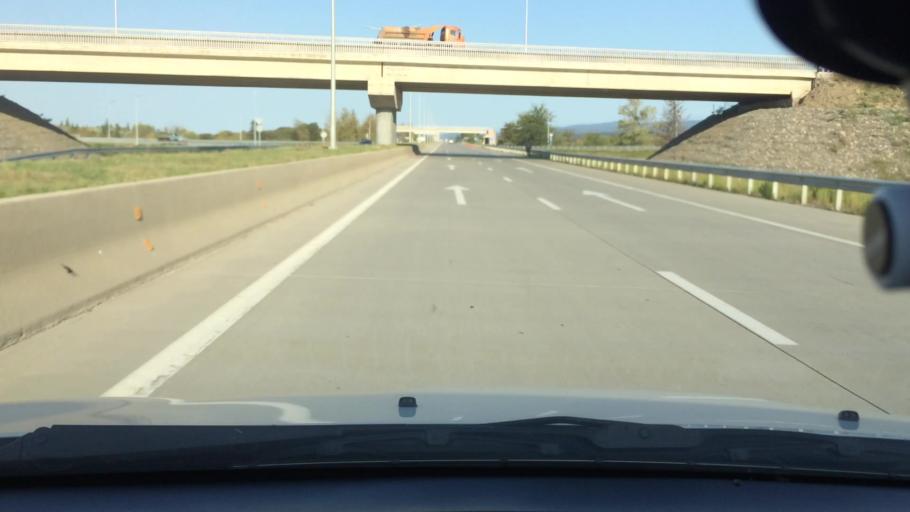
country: GE
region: Imereti
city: Zestap'oni
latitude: 42.1585
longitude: 42.9508
